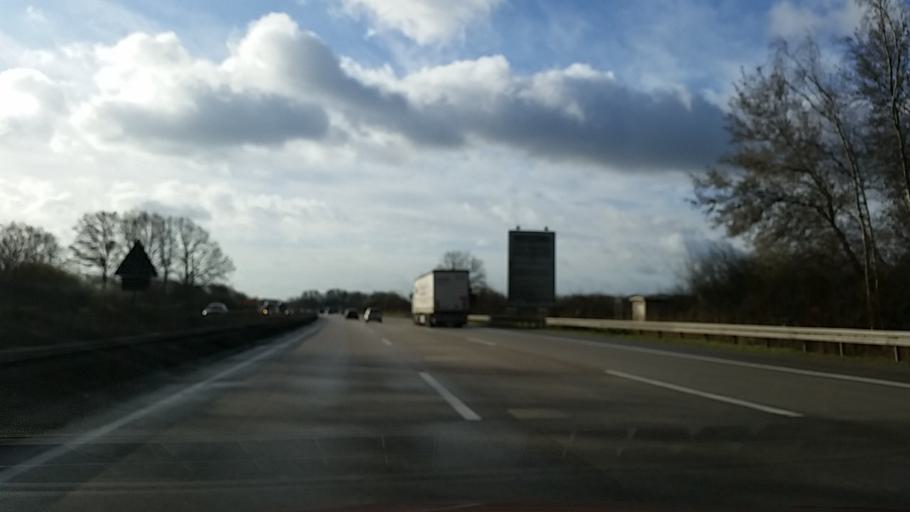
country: DE
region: Lower Saxony
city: Isernhagen Farster Bauerschaft
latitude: 52.4547
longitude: 9.8605
